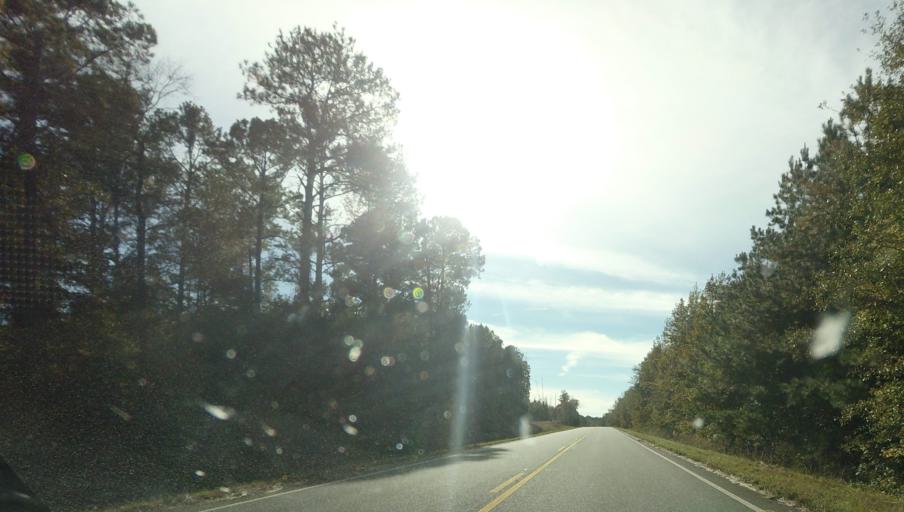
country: US
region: Georgia
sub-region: Upson County
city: Thomaston
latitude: 32.7172
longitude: -84.3466
